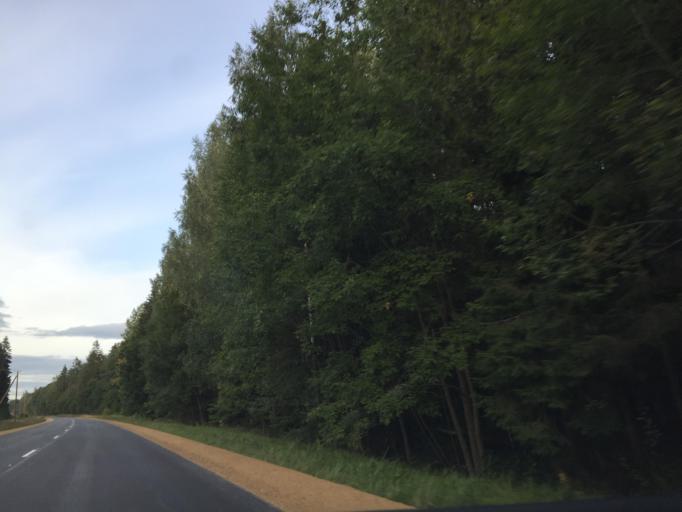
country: LV
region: Viesite
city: Viesite
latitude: 56.3792
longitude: 25.6645
